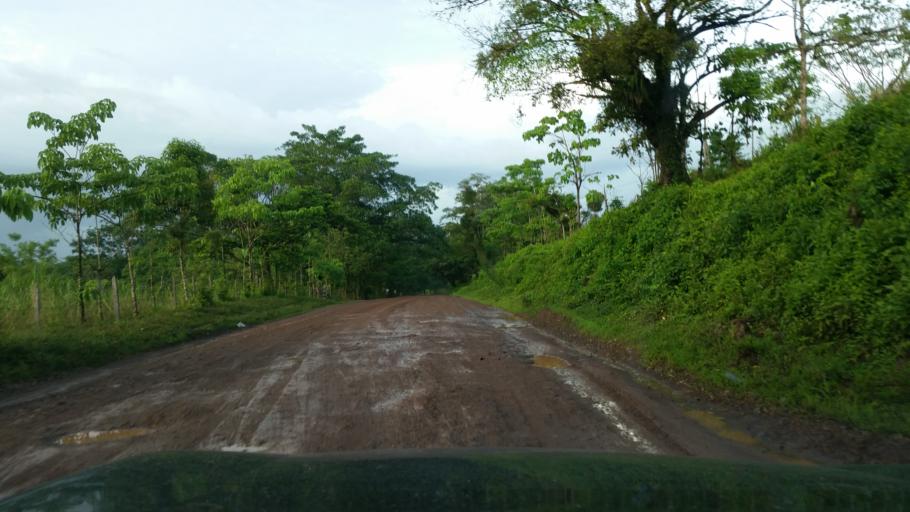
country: NI
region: Atlantico Norte (RAAN)
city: Siuna
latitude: 13.3650
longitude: -84.8801
